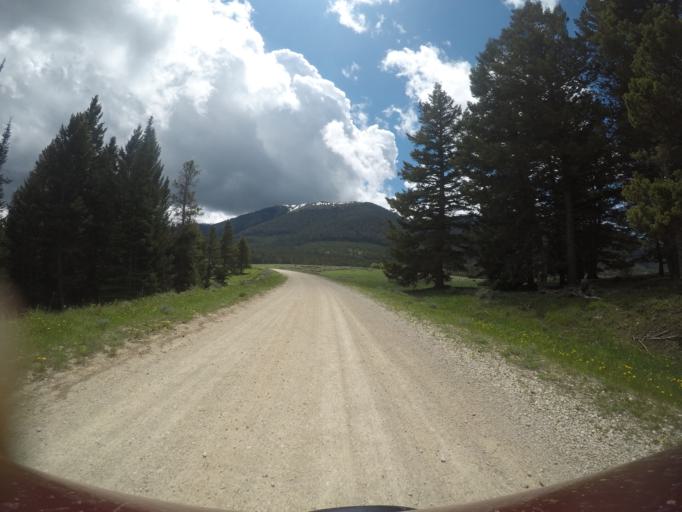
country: US
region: Wyoming
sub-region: Big Horn County
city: Lovell
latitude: 45.1762
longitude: -108.4515
